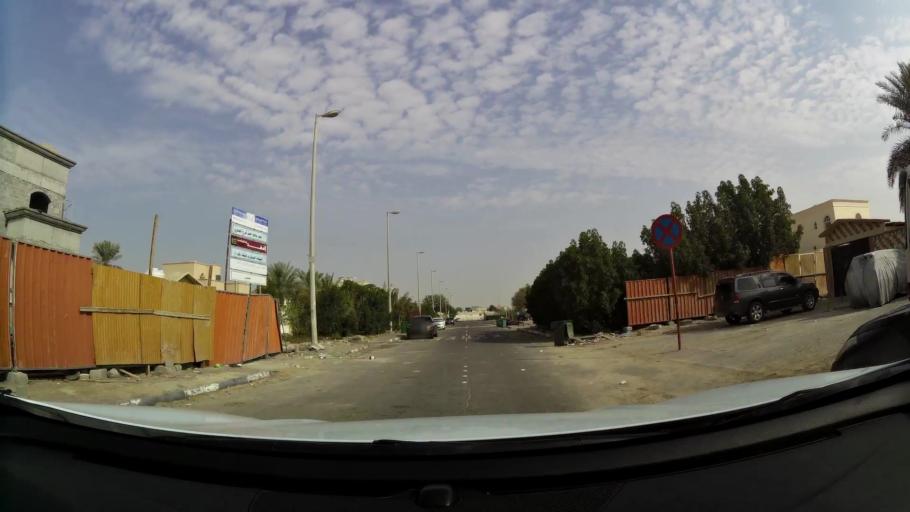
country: AE
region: Abu Dhabi
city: Abu Dhabi
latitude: 24.2607
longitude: 54.7008
